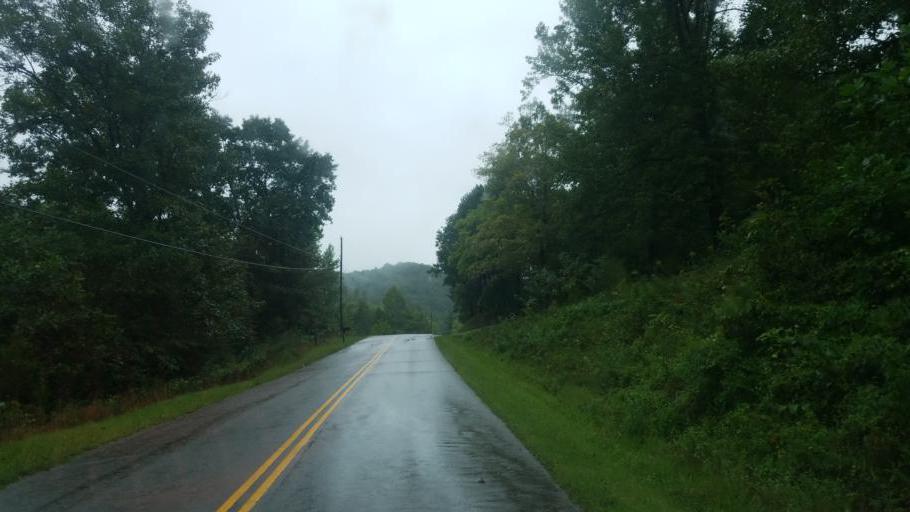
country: US
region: Ohio
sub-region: Scioto County
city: West Portsmouth
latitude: 38.7476
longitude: -83.0919
